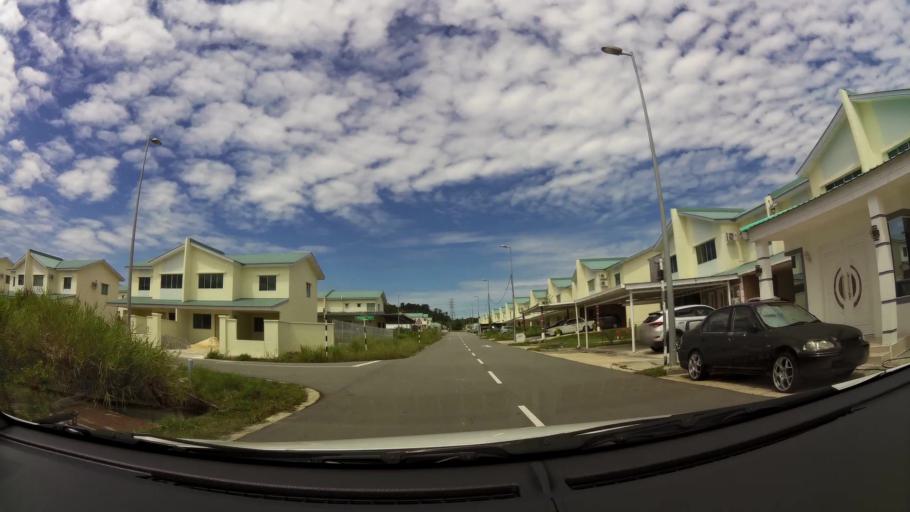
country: BN
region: Brunei and Muara
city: Bandar Seri Begawan
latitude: 4.9732
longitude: 115.0096
